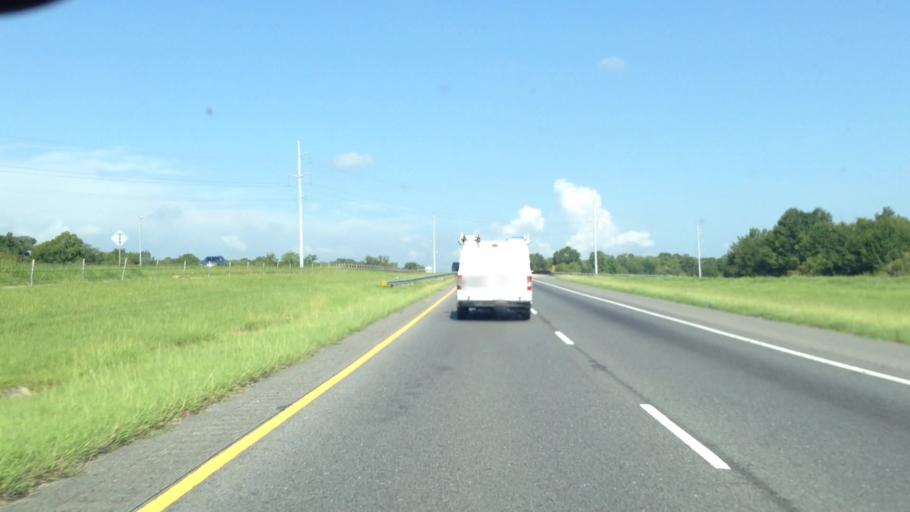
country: US
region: Louisiana
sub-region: Ascension Parish
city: Sorrento
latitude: 30.1533
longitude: -90.8035
